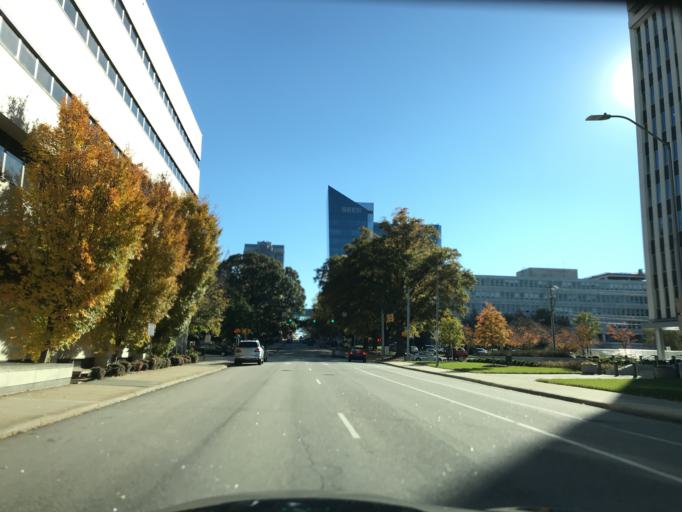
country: US
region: North Carolina
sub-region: Wake County
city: Raleigh
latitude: 35.7847
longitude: -78.6399
